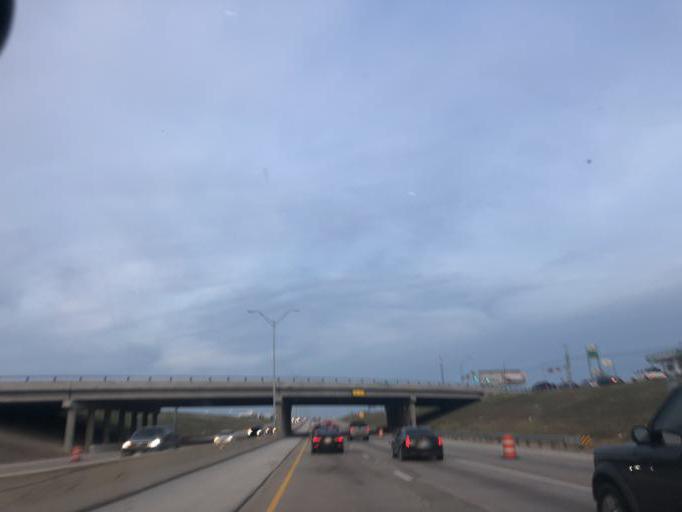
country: US
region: Texas
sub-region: Dallas County
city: Duncanville
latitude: 32.6704
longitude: -96.8625
